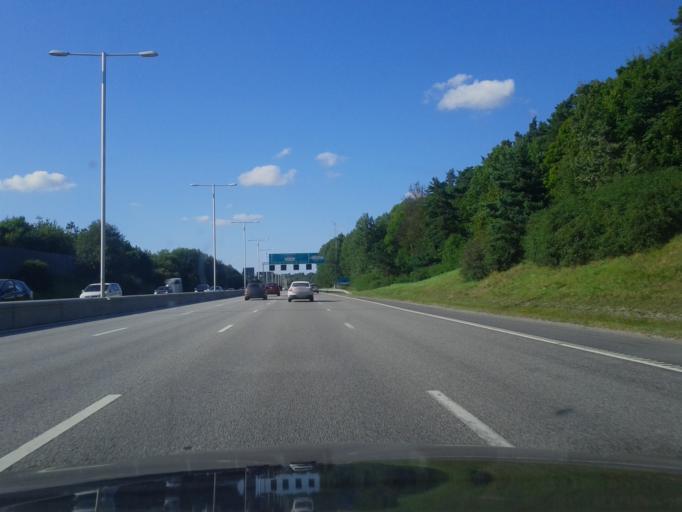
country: SE
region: Stockholm
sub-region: Solna Kommun
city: Solna
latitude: 59.3829
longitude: 18.0077
